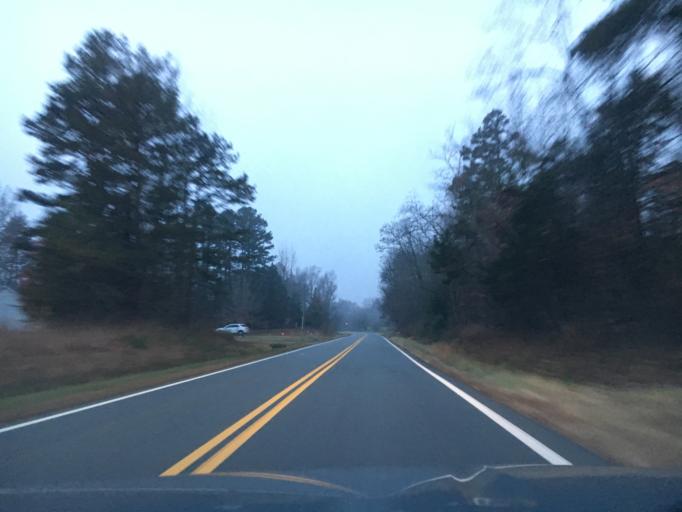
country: US
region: Virginia
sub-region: Halifax County
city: Mountain Road
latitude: 36.6884
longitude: -78.9840
